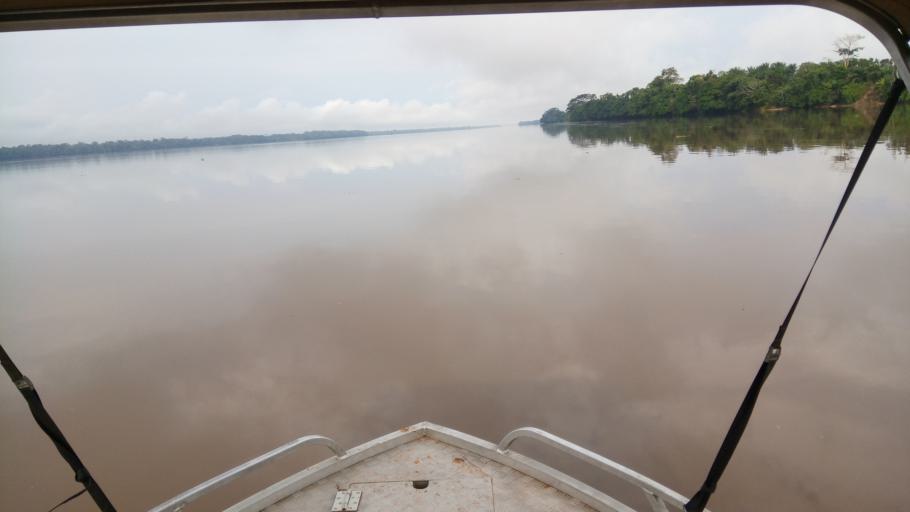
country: CD
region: Eastern Province
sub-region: Sous-Region de la Tshopo
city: Yangambi
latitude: 0.6277
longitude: 24.6946
